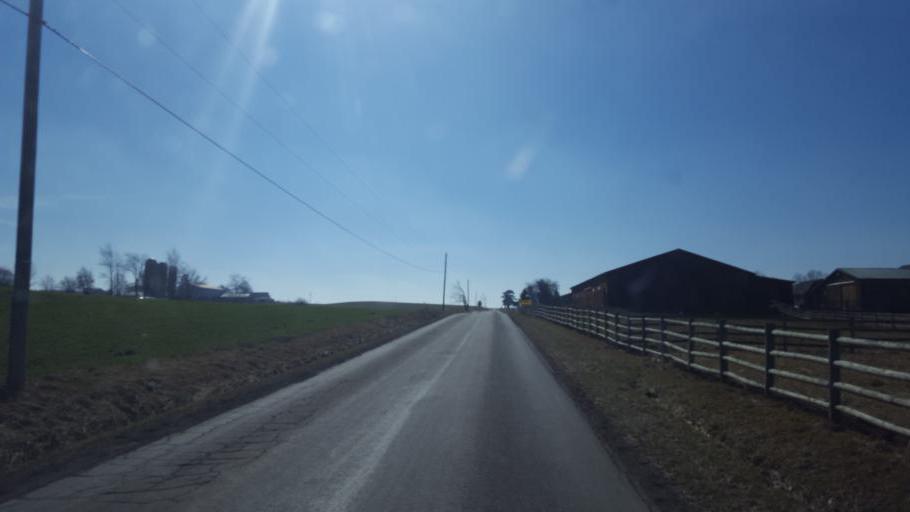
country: US
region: Ohio
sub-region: Huron County
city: Greenwich
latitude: 40.9796
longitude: -82.5820
